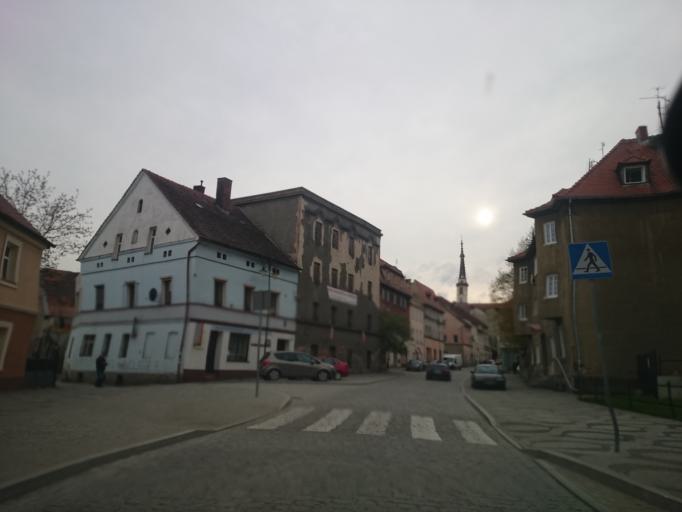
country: PL
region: Lower Silesian Voivodeship
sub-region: Powiat zabkowicki
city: Zabkowice Slaskie
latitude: 50.5888
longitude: 16.8155
